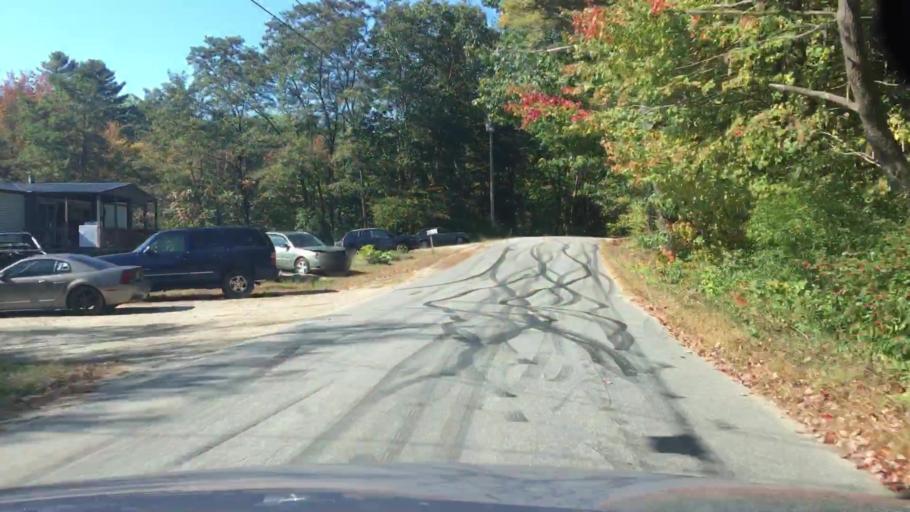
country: US
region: Maine
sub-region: Androscoggin County
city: Lisbon Falls
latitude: 44.0176
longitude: -69.9841
